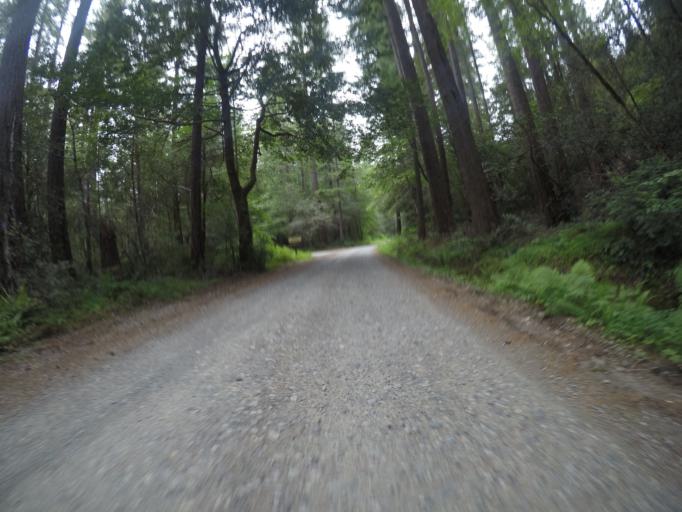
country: US
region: California
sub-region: Del Norte County
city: Bertsch-Oceanview
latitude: 41.6867
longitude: -123.9086
